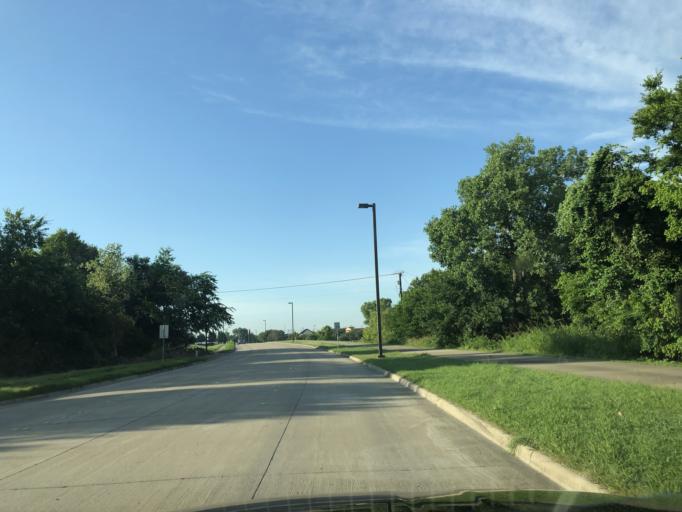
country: US
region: Texas
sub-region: Dallas County
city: Sunnyvale
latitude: 32.8423
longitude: -96.6021
